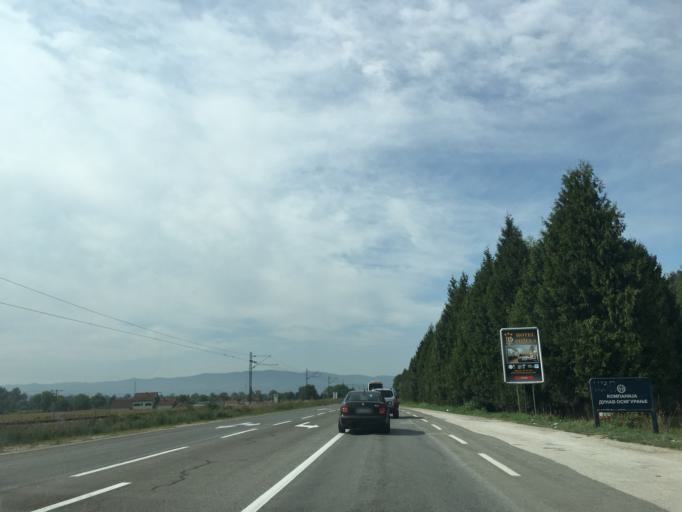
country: RS
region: Central Serbia
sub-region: Zlatiborski Okrug
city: Pozega
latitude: 43.8569
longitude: 20.0809
